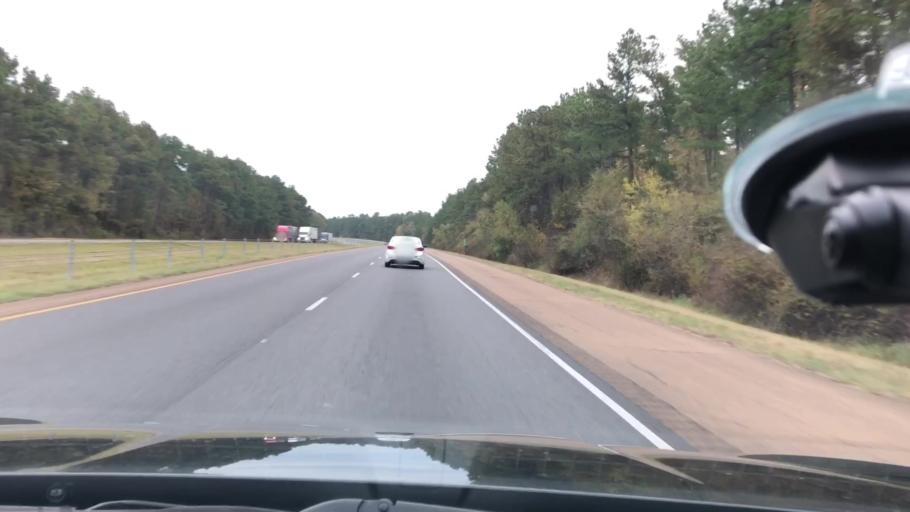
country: US
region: Arkansas
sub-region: Clark County
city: Gurdon
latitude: 33.9546
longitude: -93.2280
